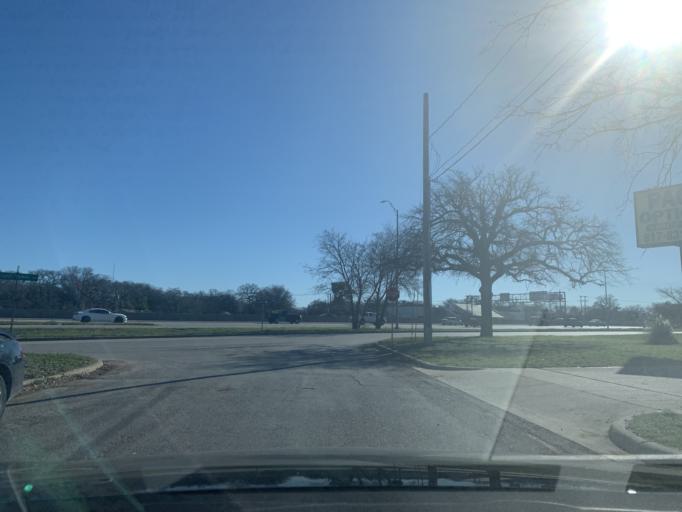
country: US
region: Texas
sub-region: Tarrant County
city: Haltom City
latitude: 32.7790
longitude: -97.2808
